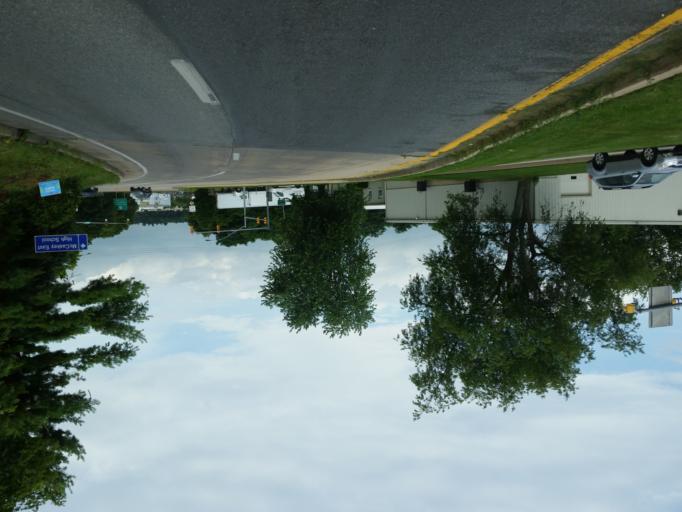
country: US
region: Pennsylvania
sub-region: Lancaster County
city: Lancaster
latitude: 40.0447
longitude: -76.2850
